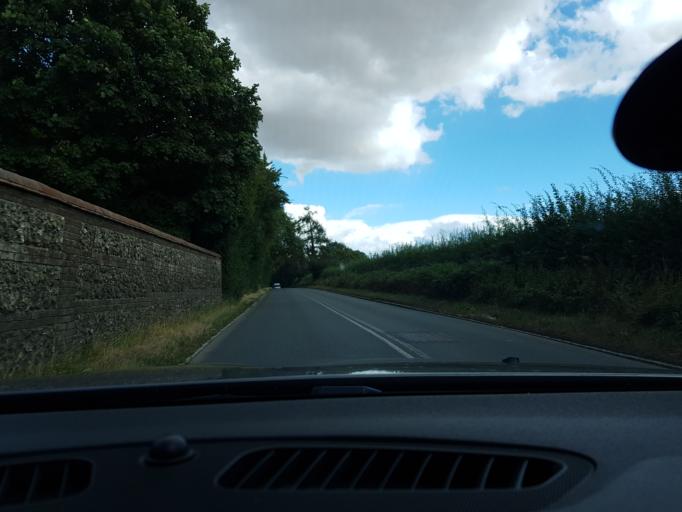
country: GB
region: England
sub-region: West Berkshire
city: Hungerford
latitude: 51.4647
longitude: -1.4959
